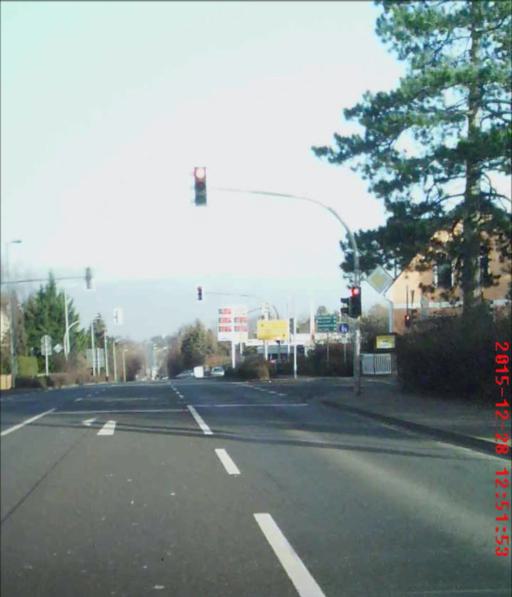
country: DE
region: Thuringia
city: Niederrossla
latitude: 51.0204
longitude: 11.4806
